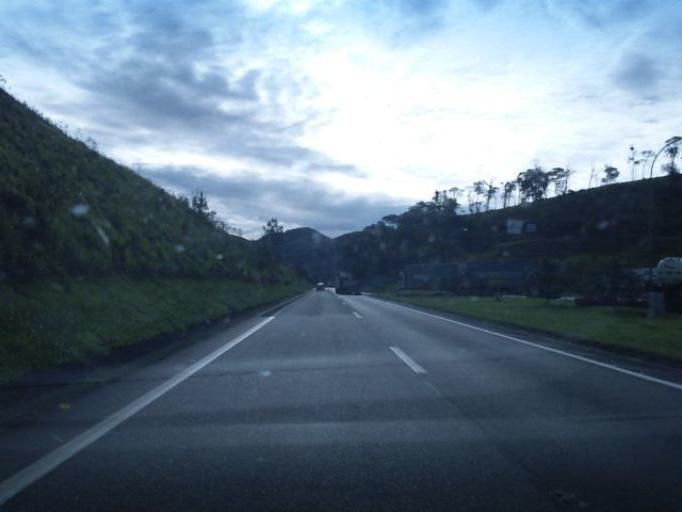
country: BR
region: Parana
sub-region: Campina Grande Do Sul
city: Campina Grande do Sul
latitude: -25.1083
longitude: -48.7942
